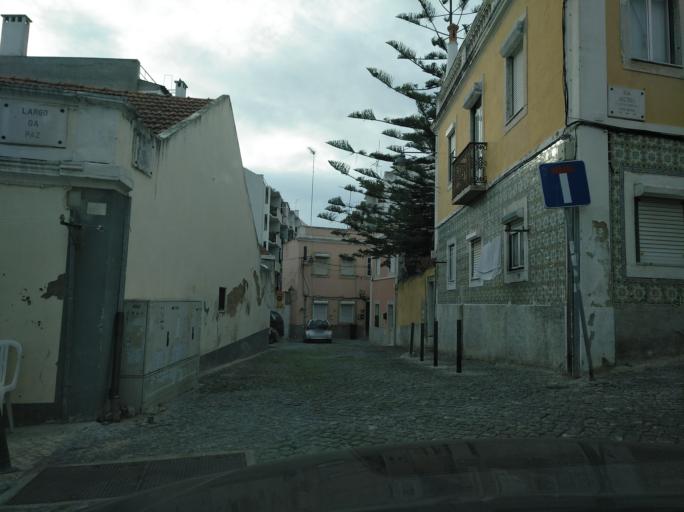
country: PT
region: Lisbon
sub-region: Oeiras
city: Alges
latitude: 38.7045
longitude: -9.2005
